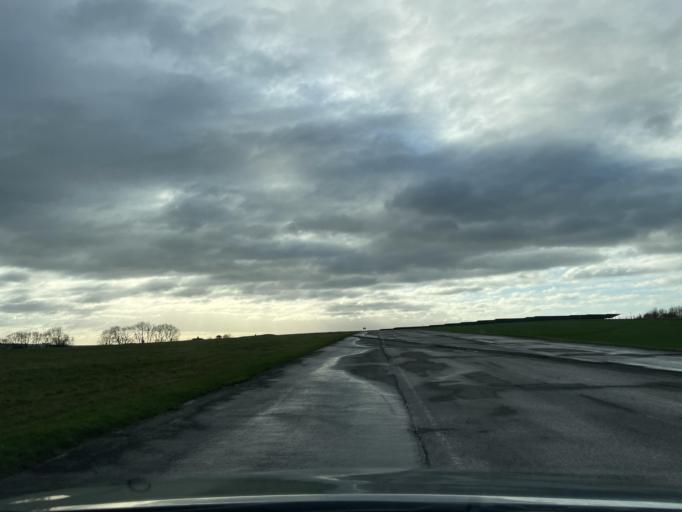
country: GB
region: England
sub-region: Borough of Swindon
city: Wroughton
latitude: 51.5081
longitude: -1.8070
